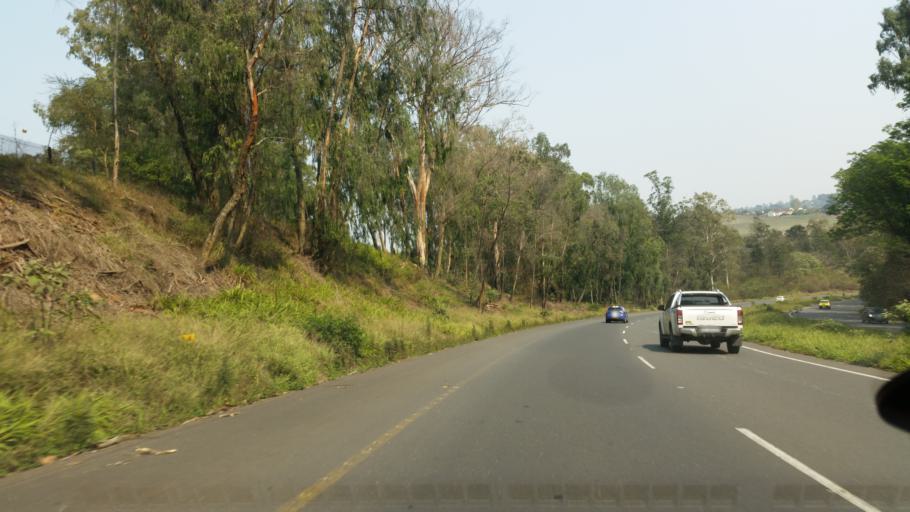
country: ZA
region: KwaZulu-Natal
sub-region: eThekwini Metropolitan Municipality
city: Mpumalanga
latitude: -29.7999
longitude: 30.7550
